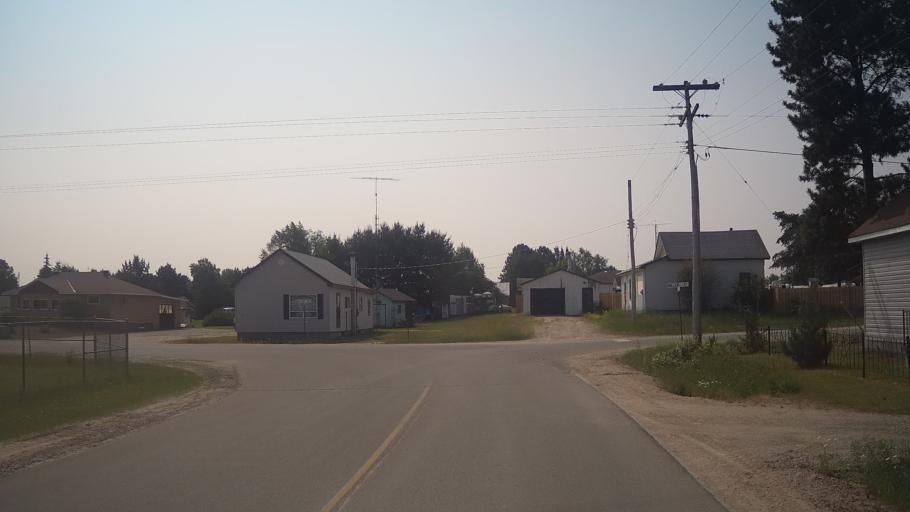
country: CA
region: Ontario
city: Timmins
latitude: 47.6740
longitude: -81.7255
